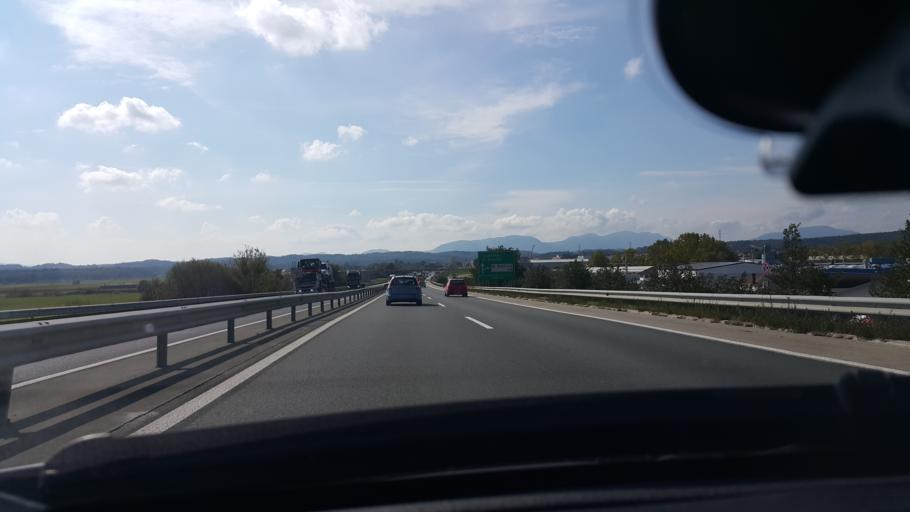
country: SI
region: Slovenska Bistrica
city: Slovenska Bistrica
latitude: 46.3903
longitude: 15.5891
